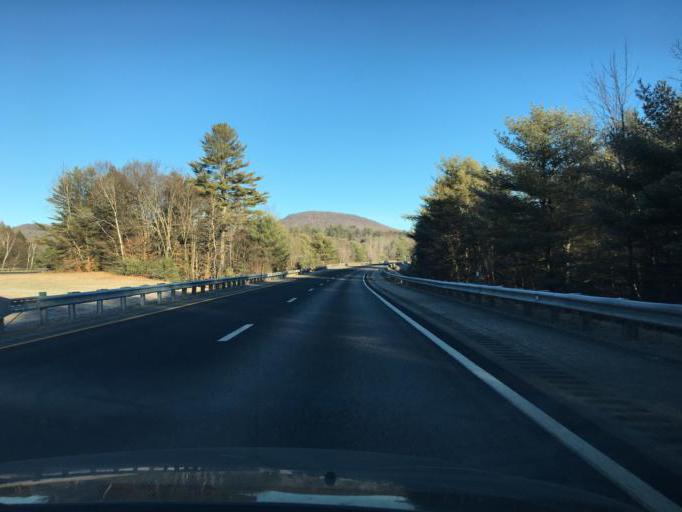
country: US
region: New Hampshire
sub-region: Grafton County
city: Plymouth
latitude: 43.7966
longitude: -71.6760
